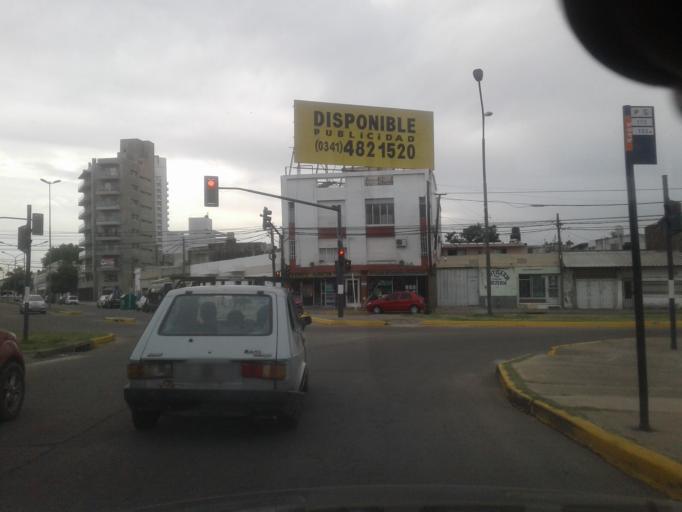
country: AR
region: Santa Fe
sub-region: Departamento de Rosario
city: Rosario
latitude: -32.9125
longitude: -60.6839
